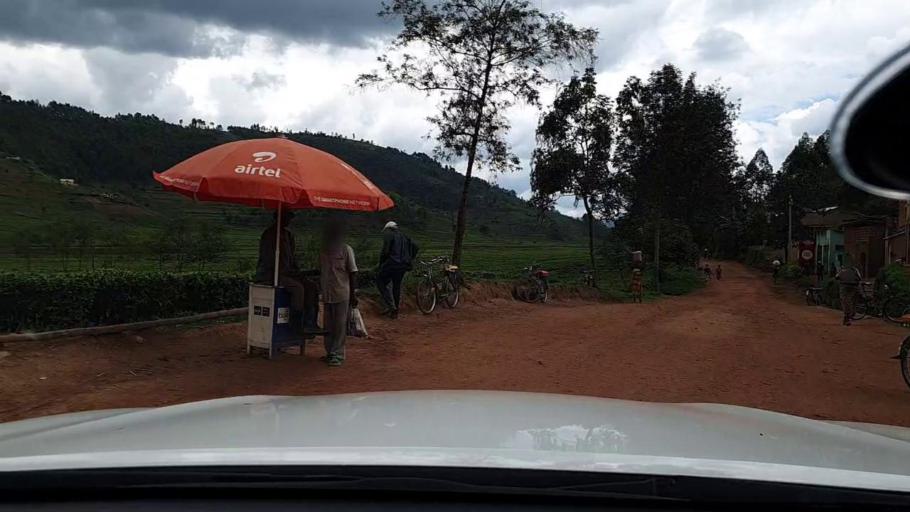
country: RW
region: Northern Province
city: Byumba
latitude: -1.6702
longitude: 29.9266
